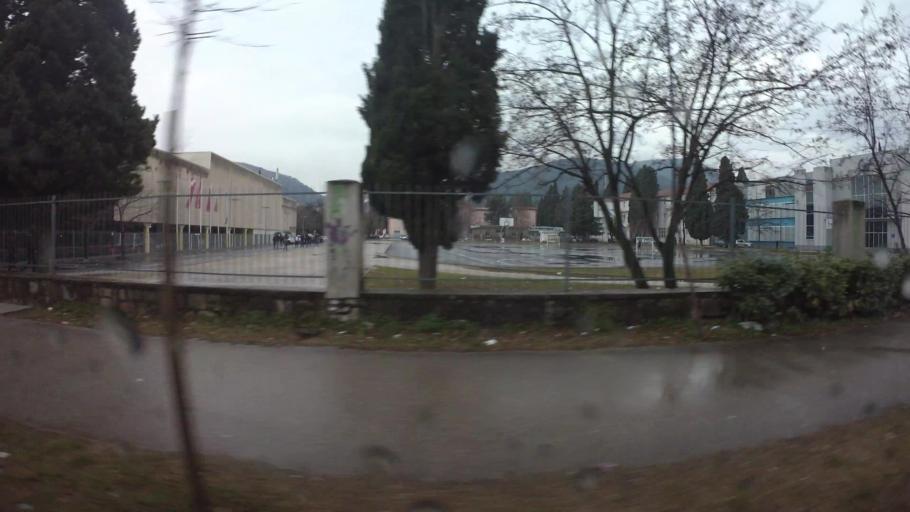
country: BA
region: Federation of Bosnia and Herzegovina
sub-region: Hercegovacko-Bosanski Kanton
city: Mostar
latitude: 43.3466
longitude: 17.7976
